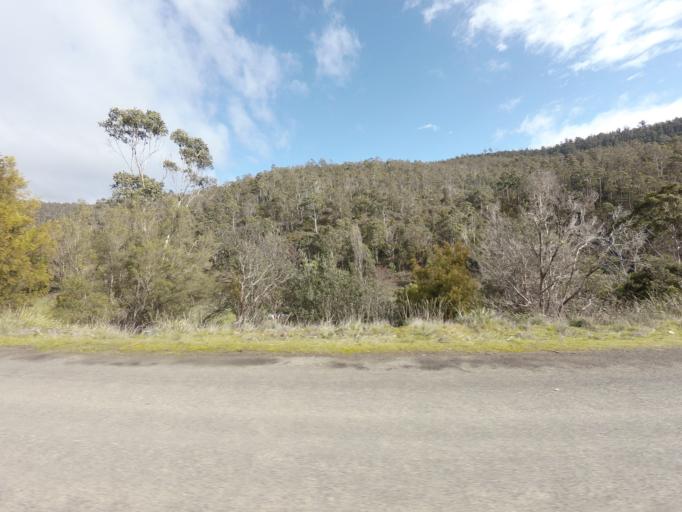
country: AU
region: Tasmania
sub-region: Derwent Valley
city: New Norfolk
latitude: -42.7866
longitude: 146.9466
